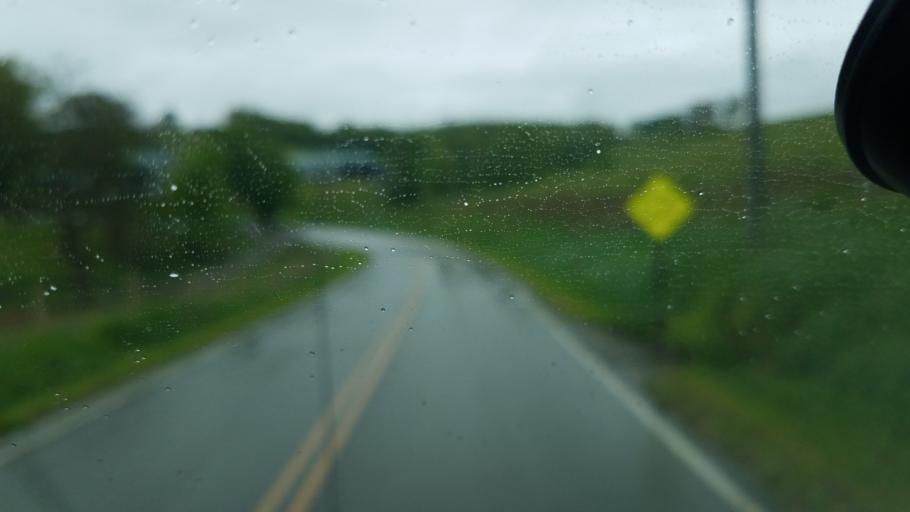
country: US
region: Ohio
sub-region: Jefferson County
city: Wintersville
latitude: 40.2696
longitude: -80.8008
